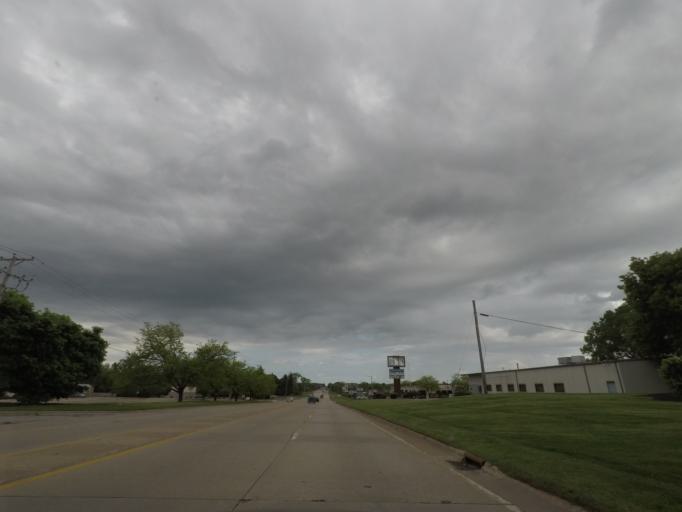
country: US
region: Illinois
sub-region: Winnebago County
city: Rockford
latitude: 42.2262
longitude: -89.0287
